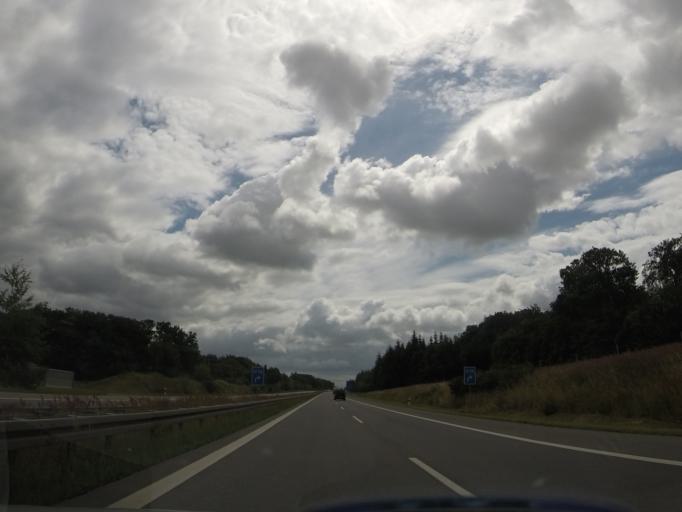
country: DE
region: Mecklenburg-Vorpommern
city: Laage
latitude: 53.9006
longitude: 12.2497
